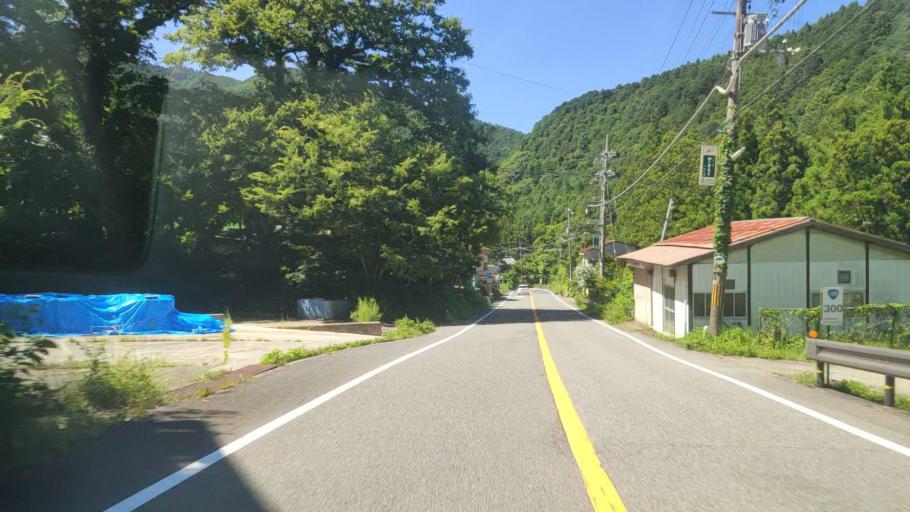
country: JP
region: Nara
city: Yoshino-cho
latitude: 34.2870
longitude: 136.0029
